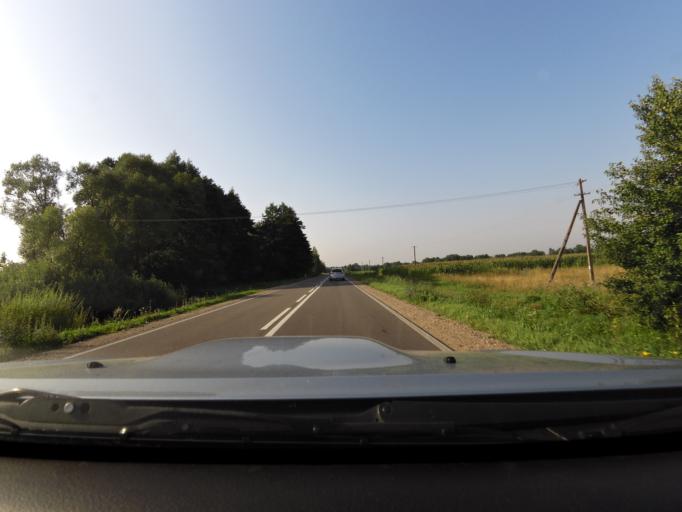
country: LT
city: Lazdijai
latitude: 54.1413
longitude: 23.4665
